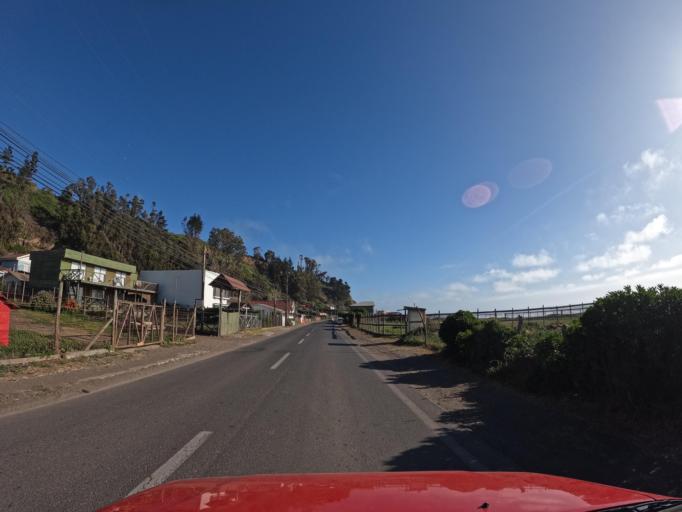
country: CL
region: Maule
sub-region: Provincia de Talca
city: Constitucion
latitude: -34.9044
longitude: -72.1801
